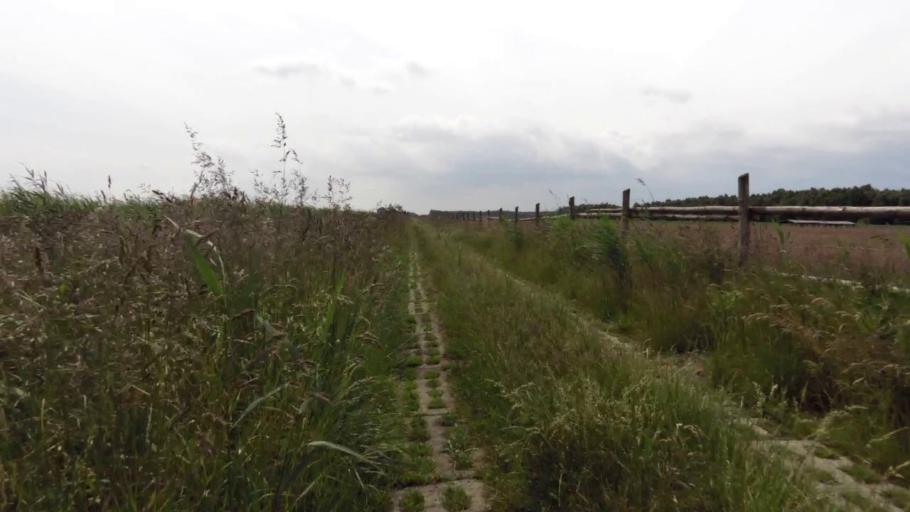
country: PL
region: West Pomeranian Voivodeship
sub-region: Powiat goleniowski
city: Stepnica
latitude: 53.7233
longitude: 14.6062
